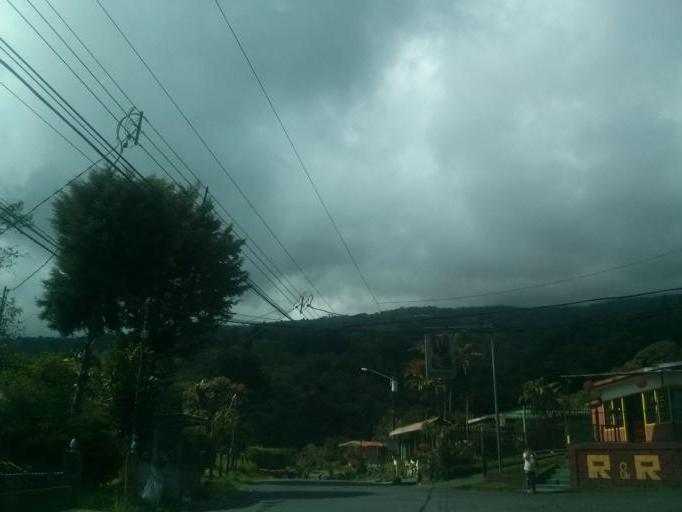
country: CR
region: Cartago
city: Turrialba
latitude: 9.9665
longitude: -83.7358
